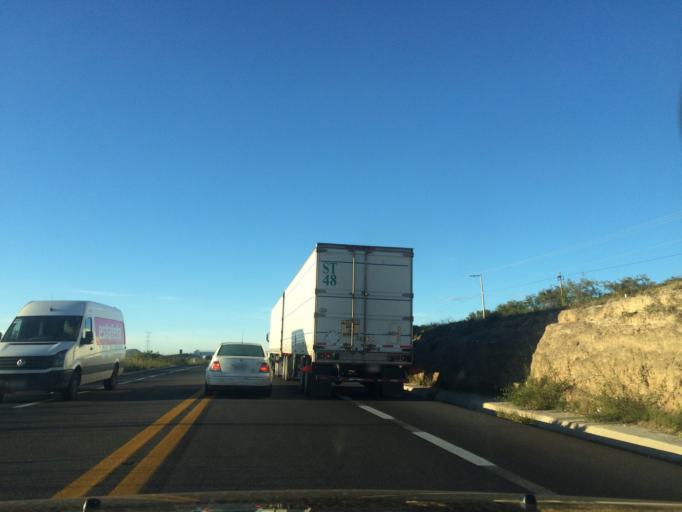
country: MX
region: Puebla
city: Morelos Canada
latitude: 18.7133
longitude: -97.4701
